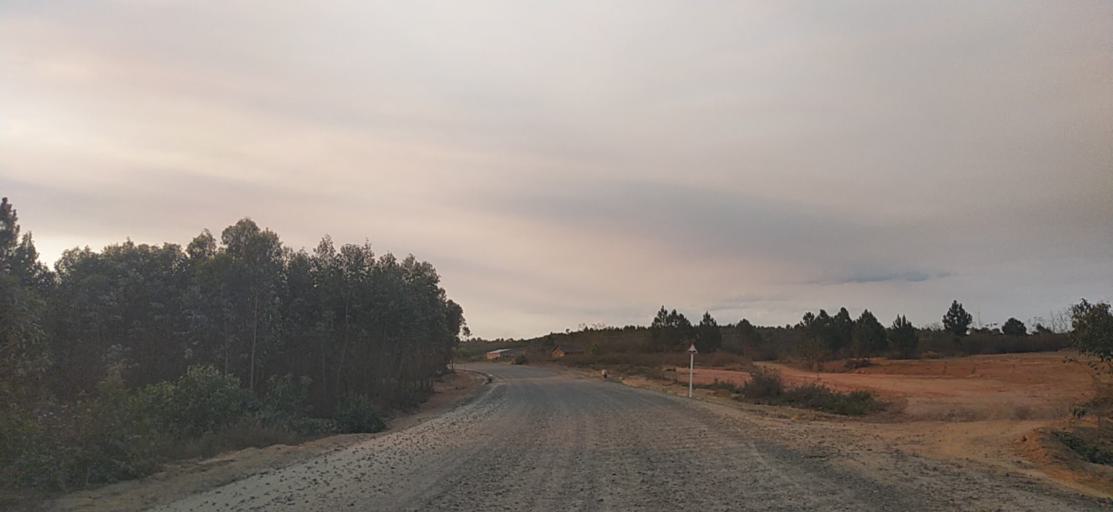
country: MG
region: Analamanga
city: Anjozorobe
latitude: -18.5010
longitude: 48.2678
